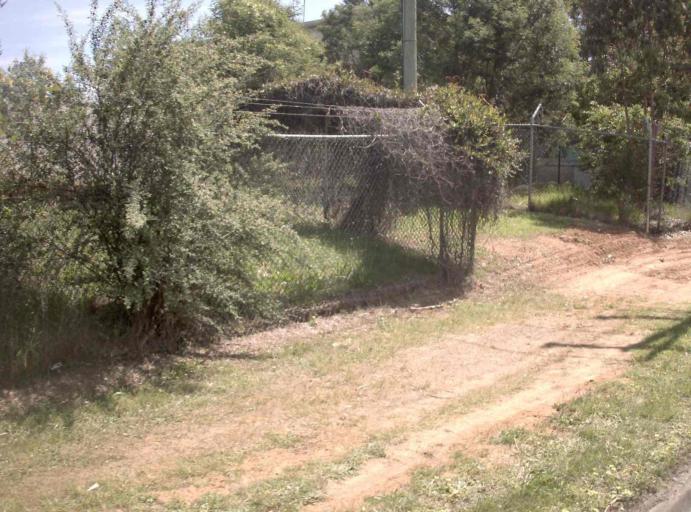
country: AU
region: Victoria
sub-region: Monash
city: Notting Hill
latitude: -37.9089
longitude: 145.1414
